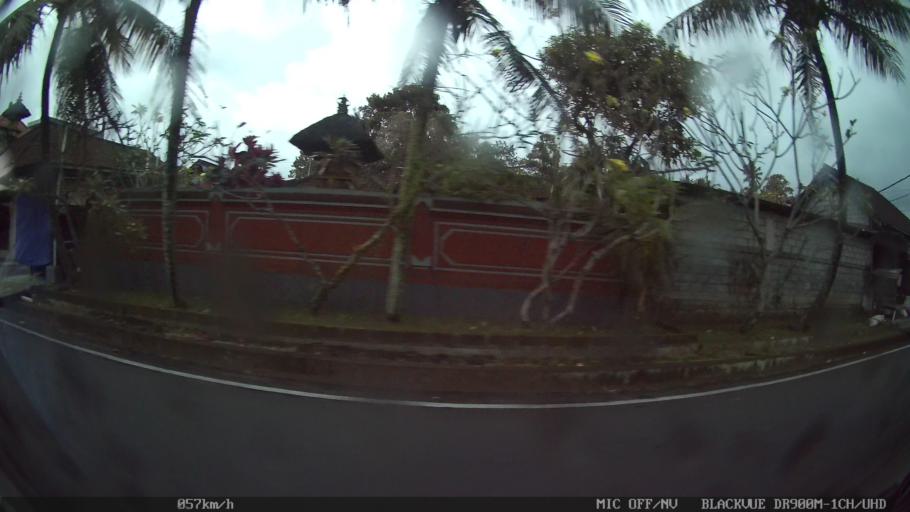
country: ID
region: Bali
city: Banjar Sayanbaleran
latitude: -8.5157
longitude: 115.1874
